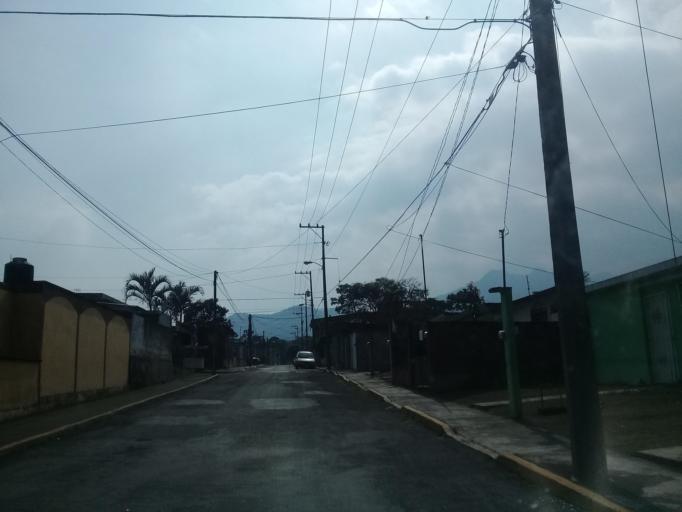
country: MX
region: Veracruz
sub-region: Mariano Escobedo
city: Palmira
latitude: 18.8753
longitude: -97.1005
